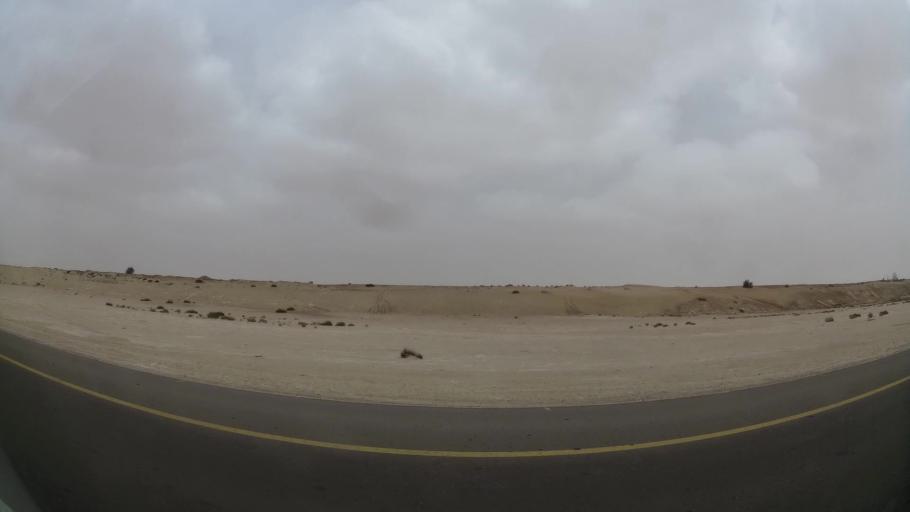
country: AE
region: Abu Dhabi
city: Abu Dhabi
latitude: 24.3999
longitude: 54.7076
